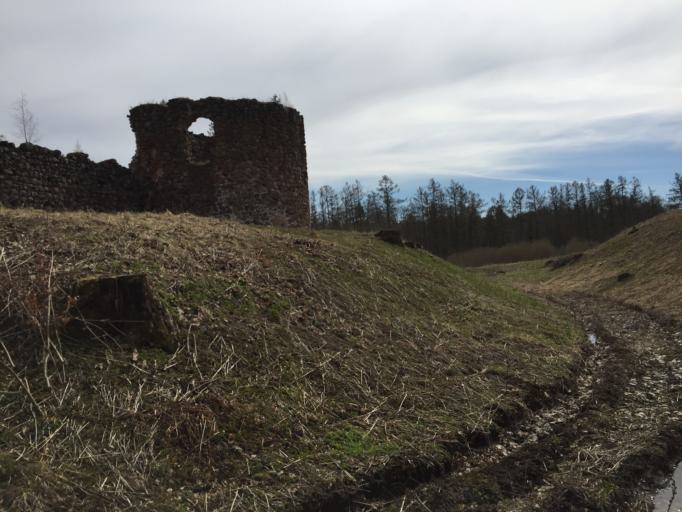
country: LV
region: Strenci
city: Seda
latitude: 57.8130
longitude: 25.8296
